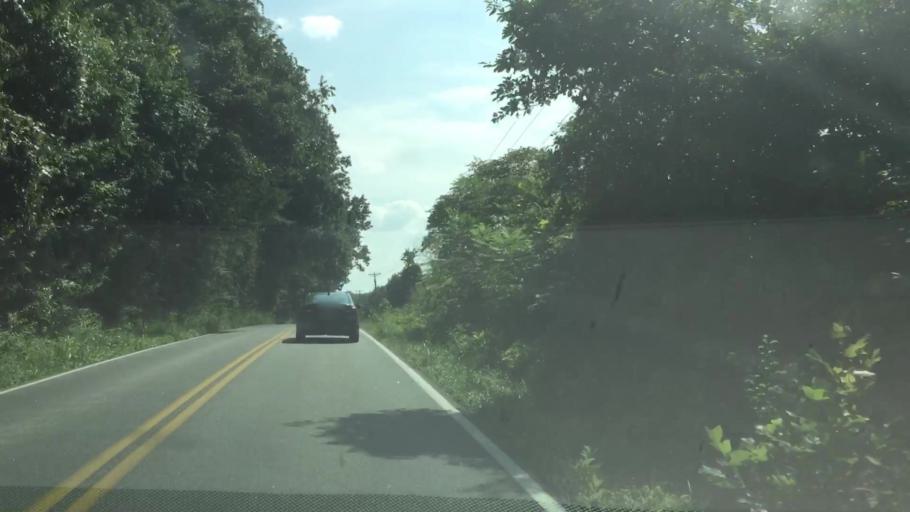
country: US
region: Tennessee
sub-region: Sullivan County
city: Fairmount
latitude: 36.6166
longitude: -82.0862
